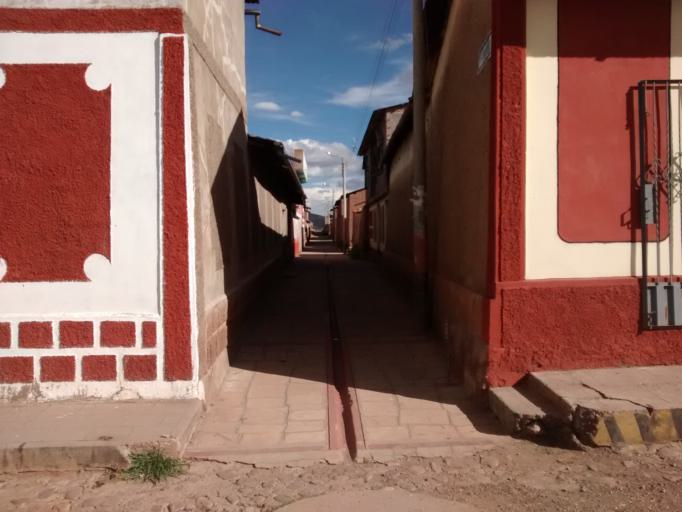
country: PE
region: Puno
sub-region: Provincia de Azangaro
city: Tirapata
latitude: -15.0423
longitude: -70.3679
